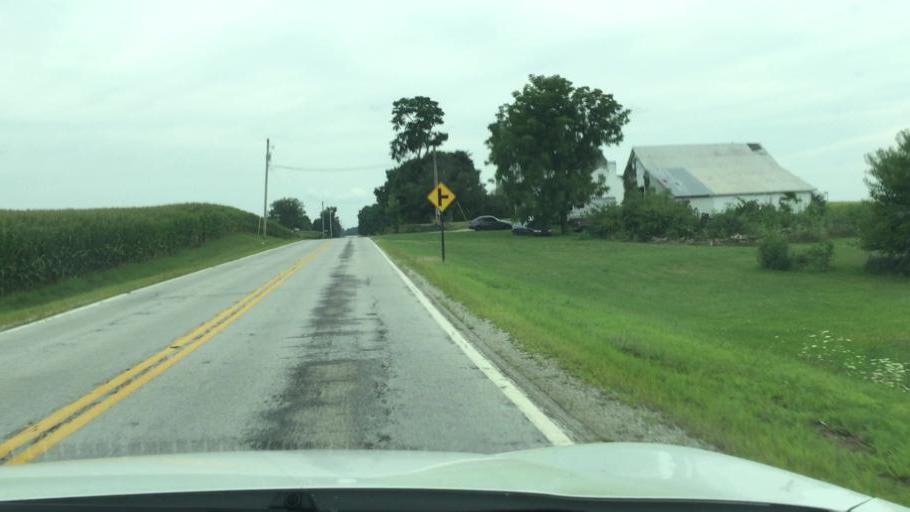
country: US
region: Ohio
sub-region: Clark County
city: Northridge
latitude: 39.9618
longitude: -83.6795
